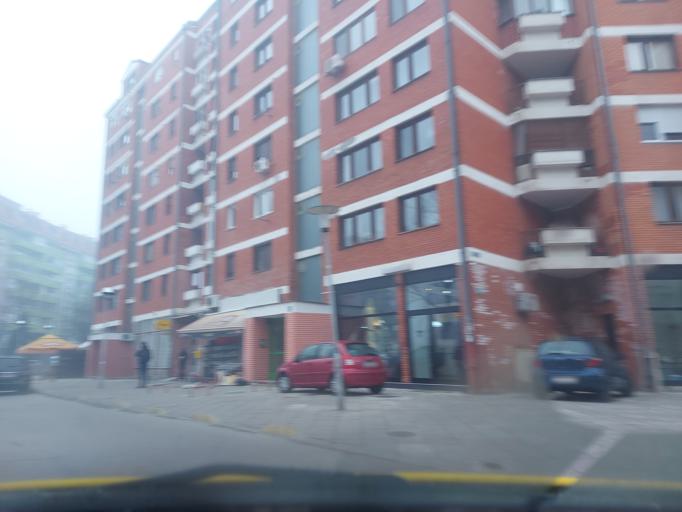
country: BA
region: Federation of Bosnia and Herzegovina
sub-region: Kanton Sarajevo
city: Sarajevo
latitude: 43.8334
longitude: 18.3426
